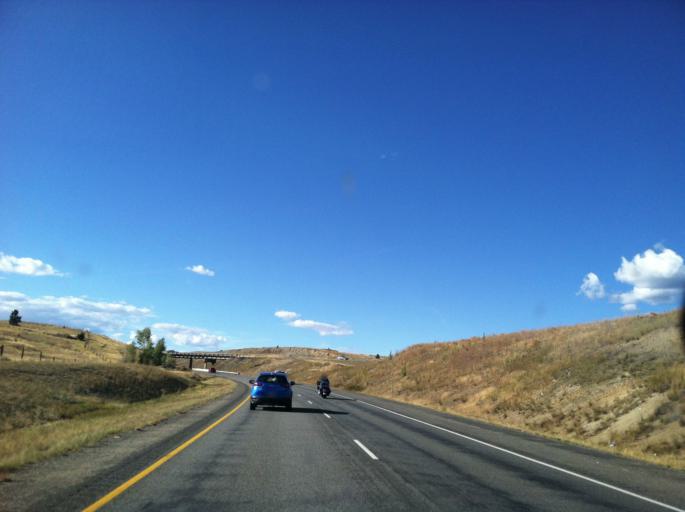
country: US
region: Montana
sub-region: Silver Bow County
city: Butte
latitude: 46.0015
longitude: -112.5671
